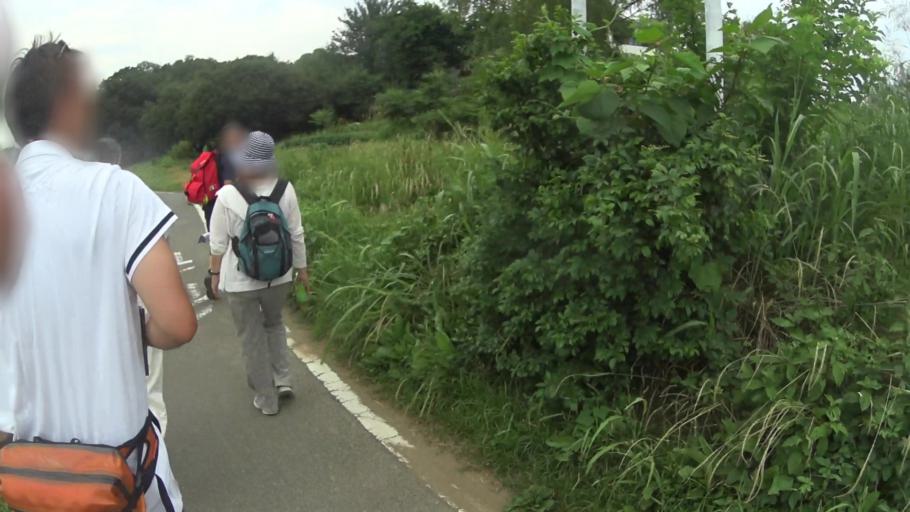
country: JP
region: Saitama
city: Okegawa
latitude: 35.9577
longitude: 139.5418
